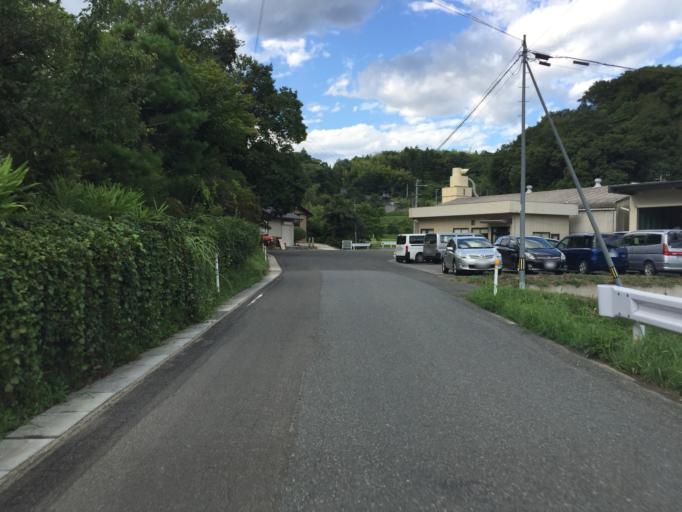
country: JP
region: Fukushima
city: Fukushima-shi
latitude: 37.6776
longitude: 140.5394
